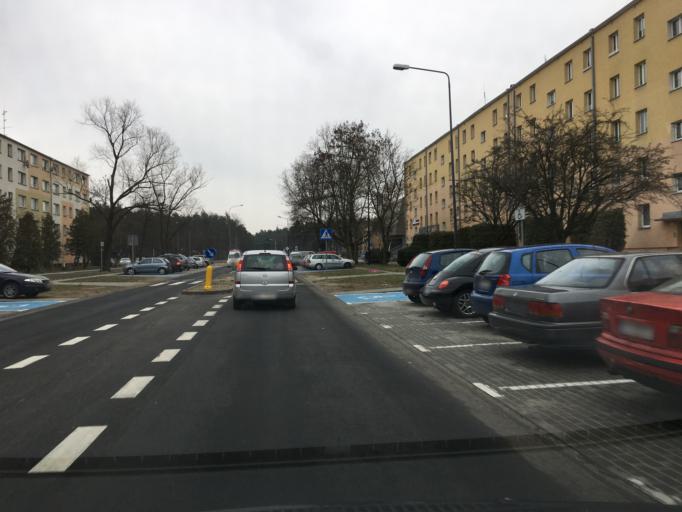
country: PL
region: Opole Voivodeship
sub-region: Powiat kedzierzynsko-kozielski
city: Kedzierzyn-Kozle
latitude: 50.3439
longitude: 18.2218
